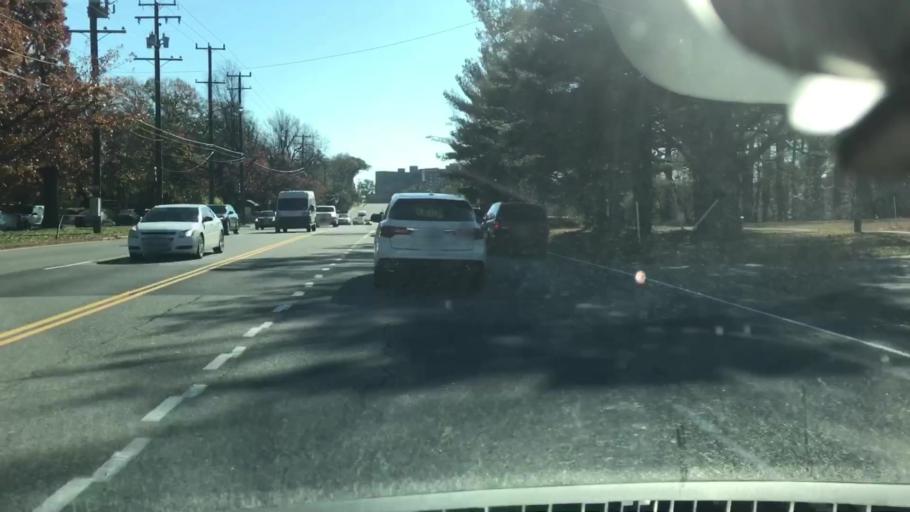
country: US
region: Virginia
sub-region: Fairfax County
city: Seven Corners
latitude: 38.8637
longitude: -77.1493
